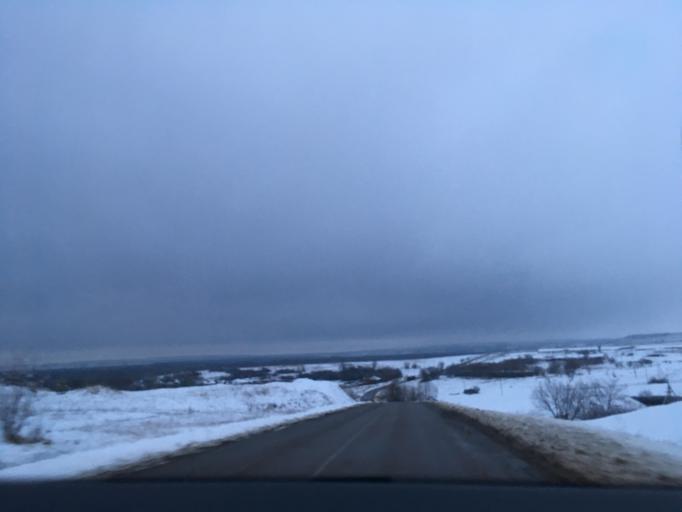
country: RU
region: Voronezj
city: Verkhniy Mamon
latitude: 50.0714
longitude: 40.3132
